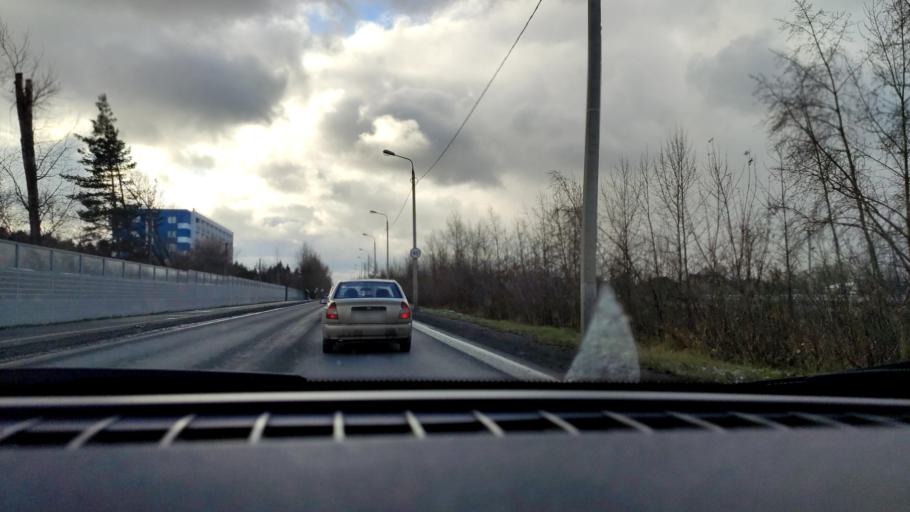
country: RU
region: Perm
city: Kondratovo
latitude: 57.9796
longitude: 56.1307
